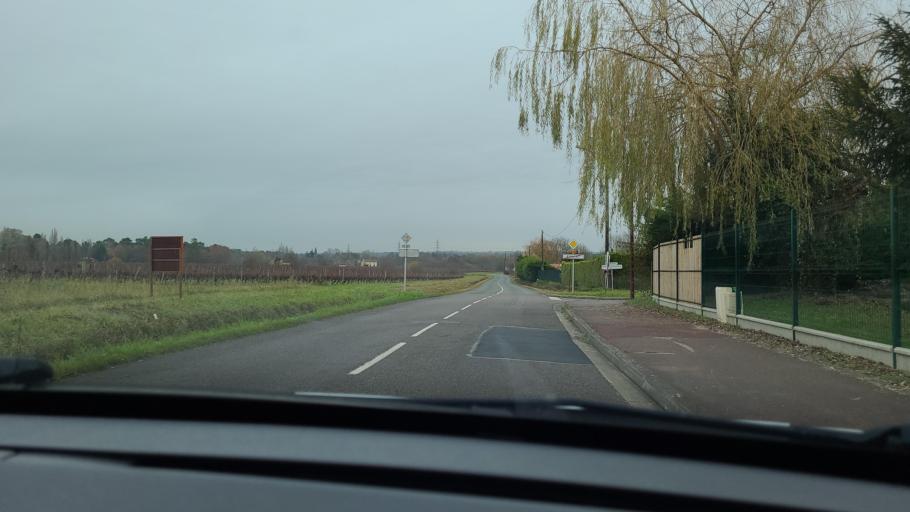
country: FR
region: Aquitaine
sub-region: Departement de la Gironde
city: Pugnac
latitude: 45.0849
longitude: -0.4896
